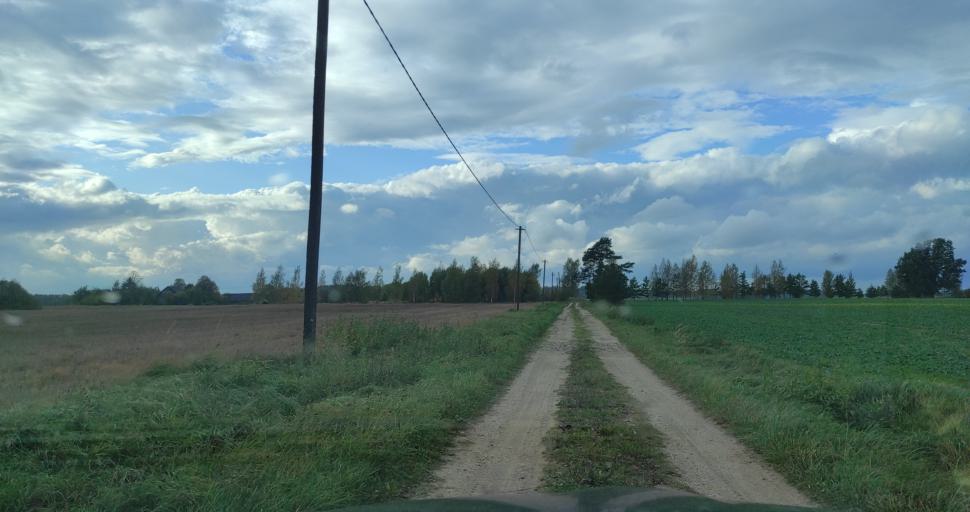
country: LV
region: Talsu Rajons
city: Sabile
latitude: 56.9003
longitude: 22.4248
